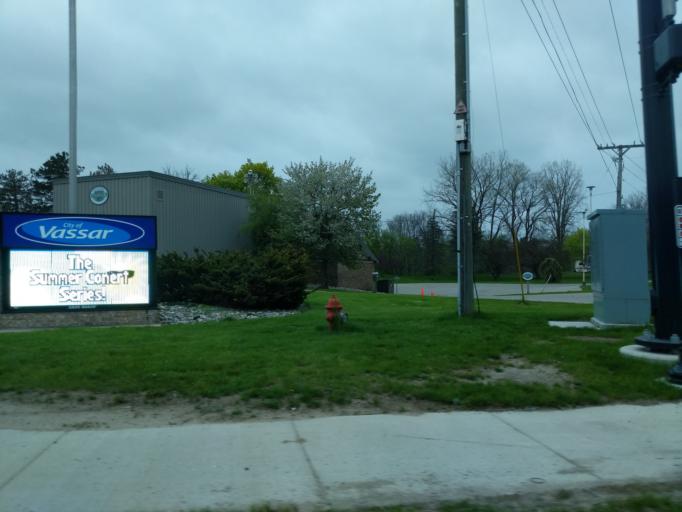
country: US
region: Michigan
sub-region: Tuscola County
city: Vassar
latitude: 43.3705
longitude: -83.5799
